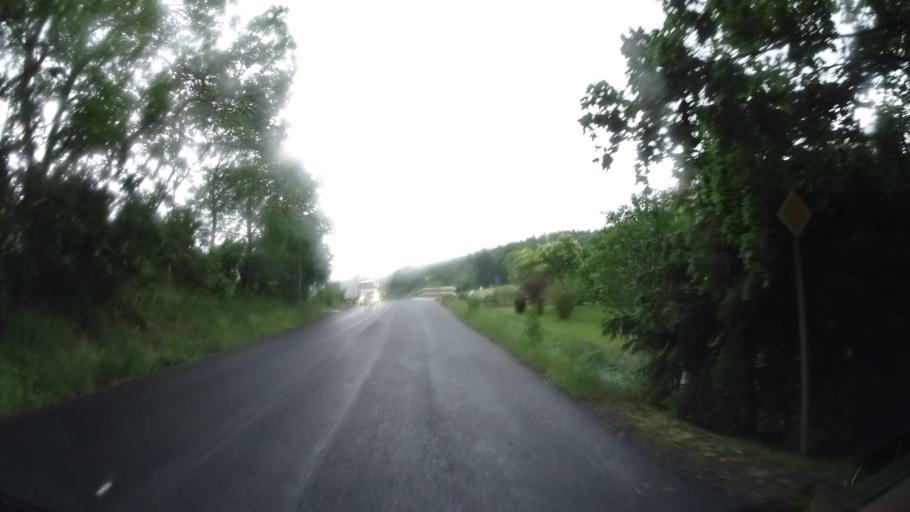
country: SE
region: Kalmar
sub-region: Oskarshamns Kommun
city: Oskarshamn
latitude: 57.3977
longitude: 16.1999
